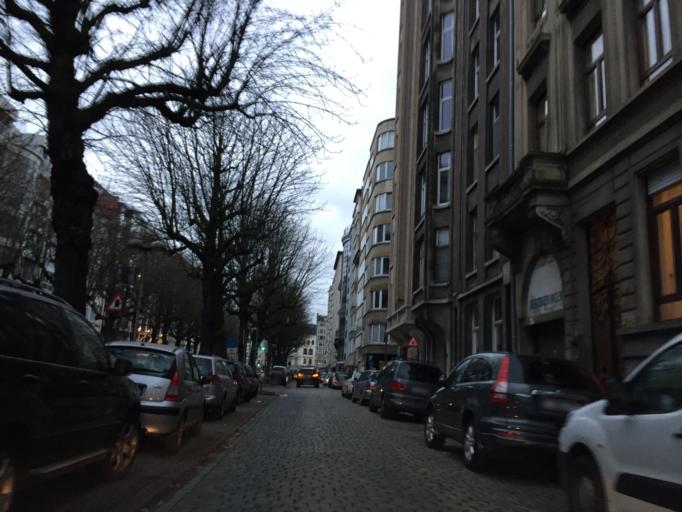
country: BE
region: Flanders
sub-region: Provincie Antwerpen
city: Antwerpen
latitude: 51.2088
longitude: 4.4184
